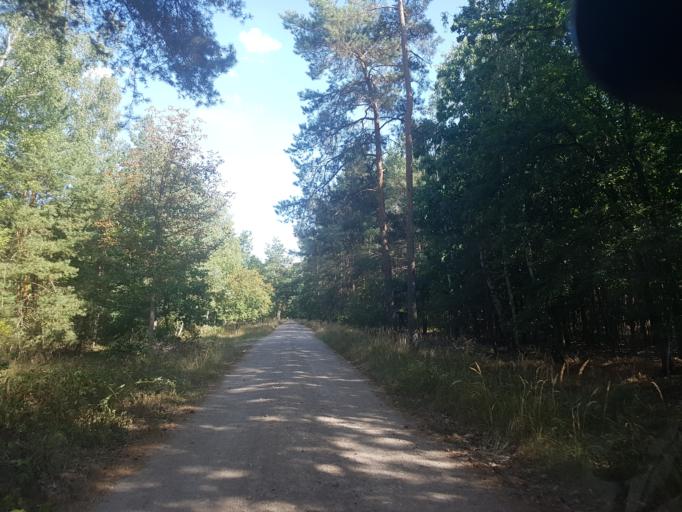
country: DE
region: Saxony-Anhalt
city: Seyda
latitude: 51.8784
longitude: 12.9506
